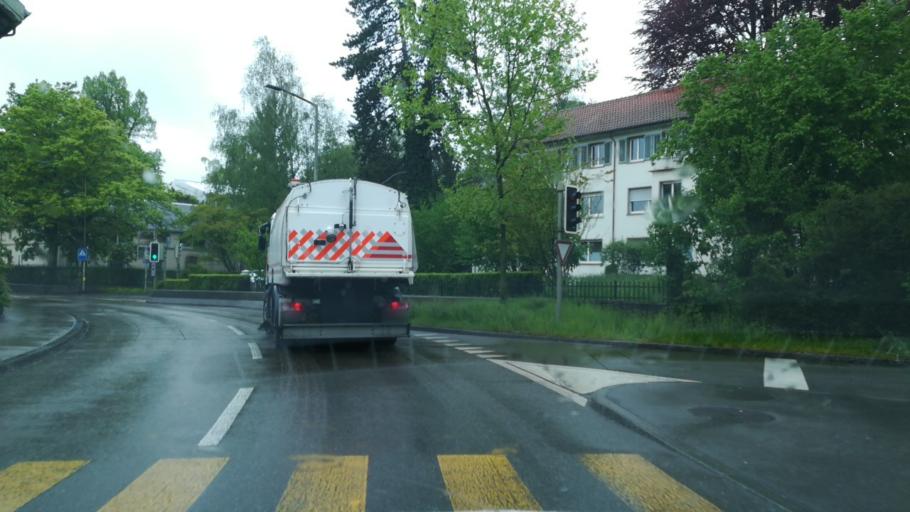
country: CH
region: Zurich
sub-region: Bezirk Winterthur
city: Stadt Winterthur (Kreis 1) / Lind
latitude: 47.5023
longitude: 8.7329
